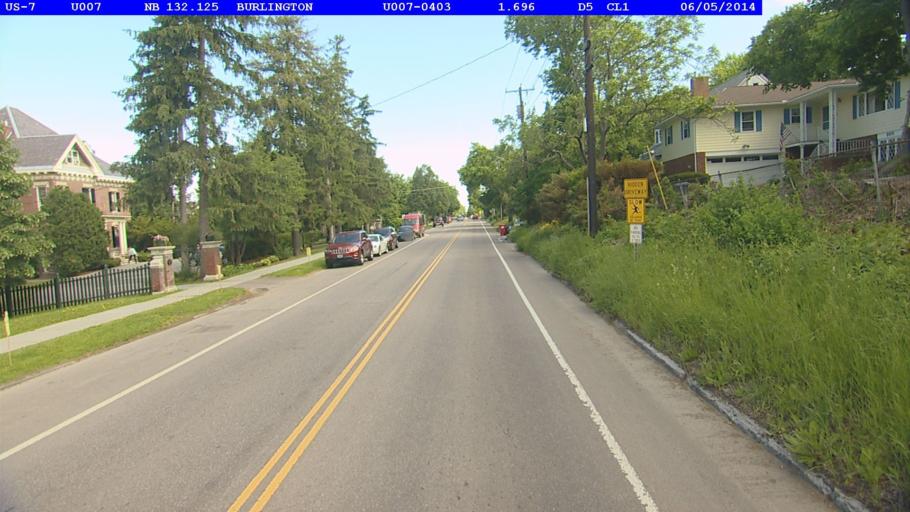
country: US
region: Vermont
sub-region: Chittenden County
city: Burlington
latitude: 44.4700
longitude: -73.2050
